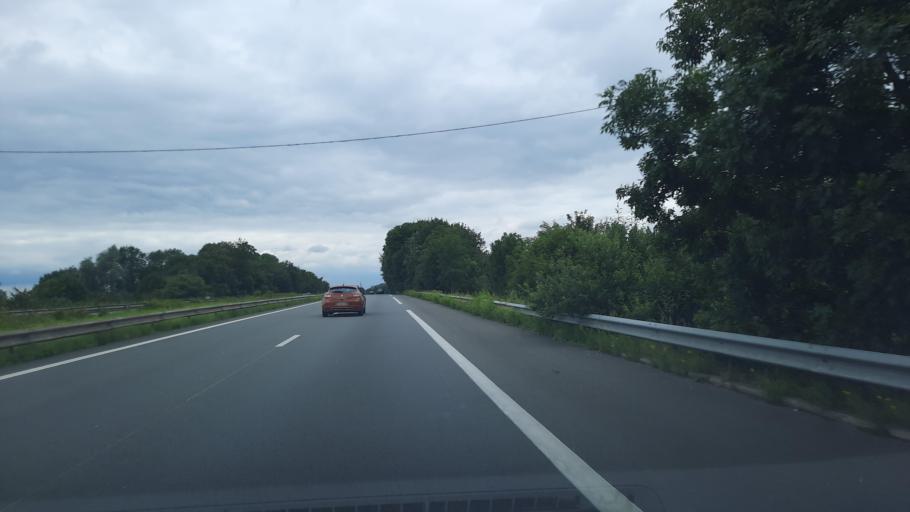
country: FR
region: Nord-Pas-de-Calais
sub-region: Departement du Nord
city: Bouvignies
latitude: 50.4594
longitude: 3.2682
